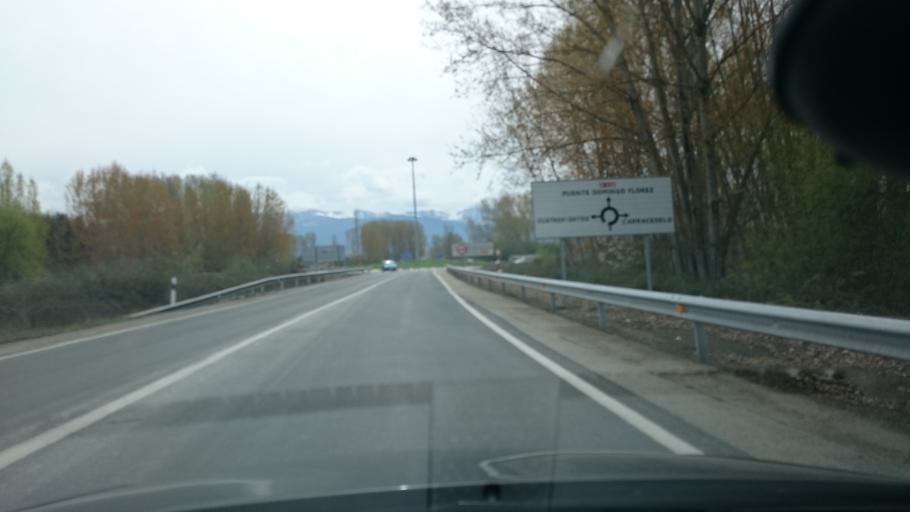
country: ES
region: Castille and Leon
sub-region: Provincia de Leon
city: Camponaraya
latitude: 42.5652
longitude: -6.6503
